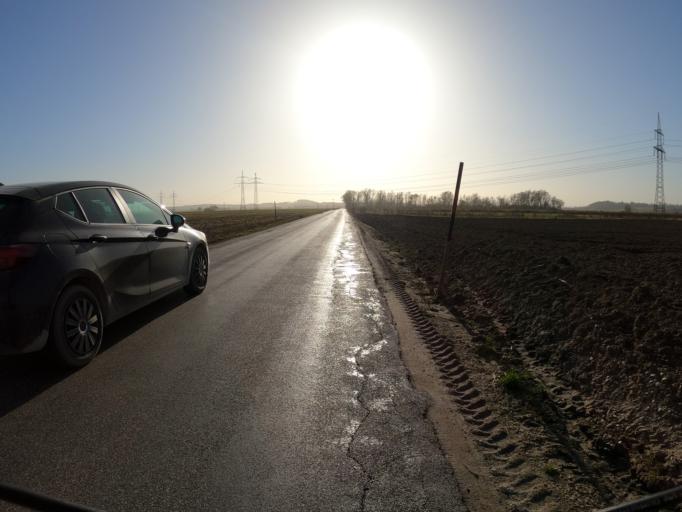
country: DE
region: Bavaria
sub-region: Swabia
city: Nersingen
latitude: 48.4091
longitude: 10.1284
